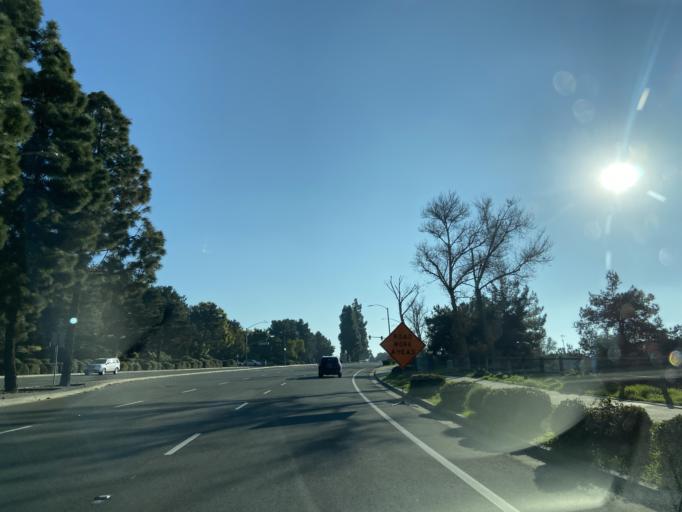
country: US
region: California
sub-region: San Diego County
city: Bonita
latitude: 32.6462
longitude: -116.9652
